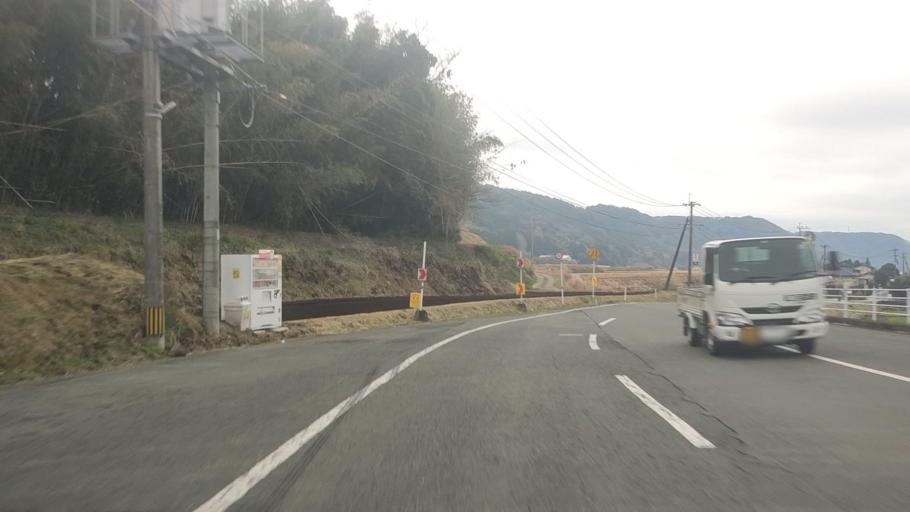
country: JP
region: Kumamoto
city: Ozu
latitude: 32.8586
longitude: 130.8932
